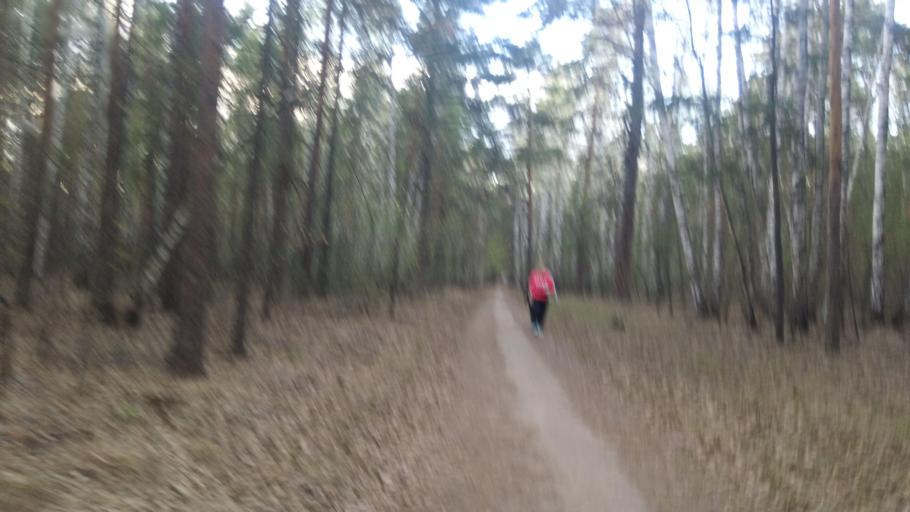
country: RU
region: Chelyabinsk
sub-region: Gorod Chelyabinsk
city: Chelyabinsk
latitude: 55.1485
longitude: 61.3375
